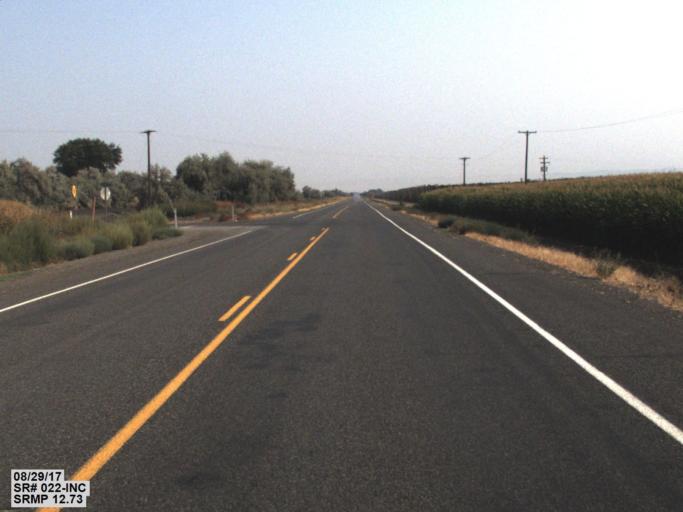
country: US
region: Washington
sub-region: Yakima County
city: Granger
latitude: 46.2904
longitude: -120.1801
